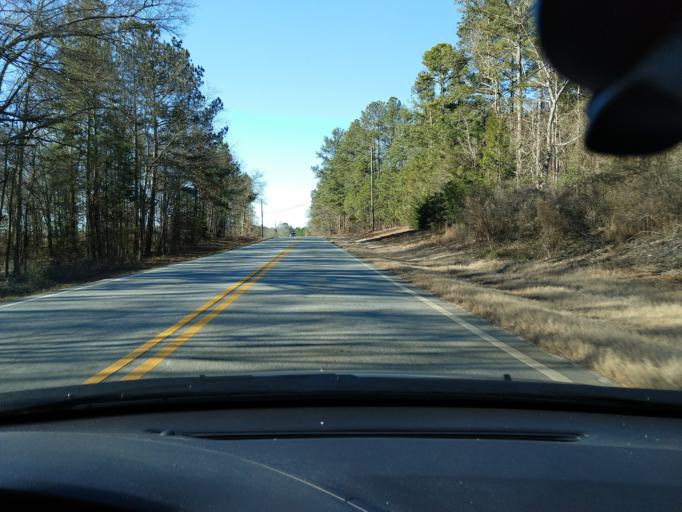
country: US
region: Georgia
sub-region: Barrow County
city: Statham
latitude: 33.9616
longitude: -83.6021
